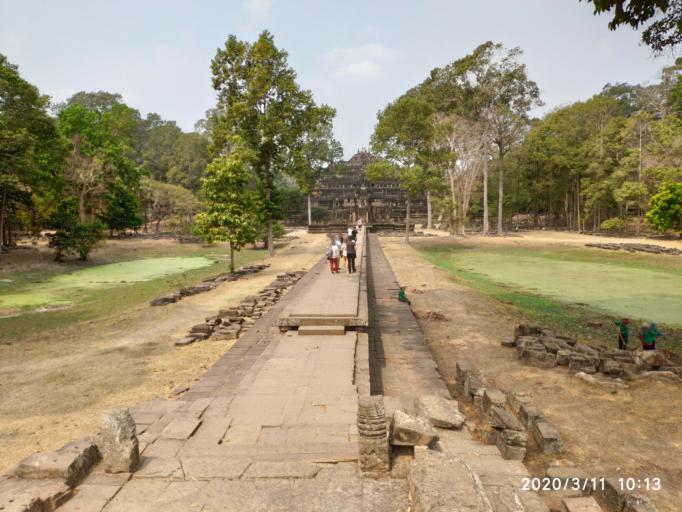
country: KH
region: Siem Reap
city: Siem Reap
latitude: 13.4439
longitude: 103.8588
